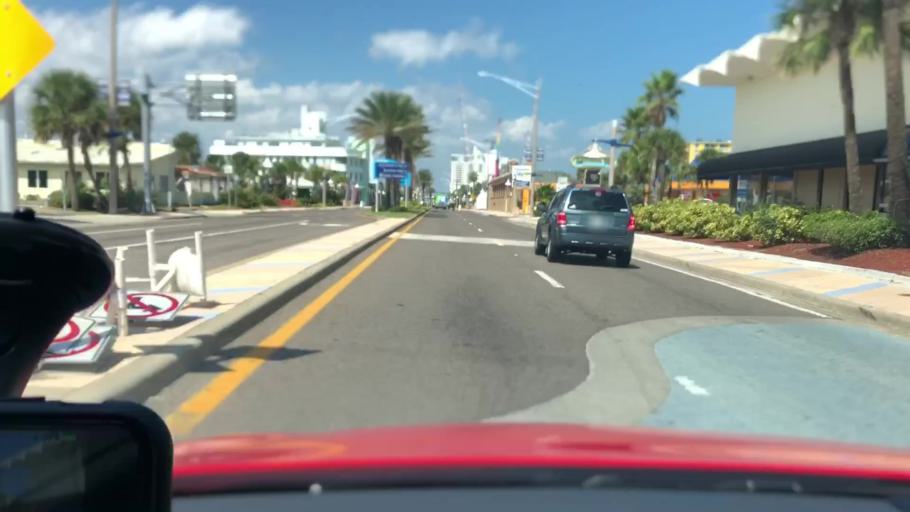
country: US
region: Florida
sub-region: Volusia County
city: Daytona Beach
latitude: 29.2221
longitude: -81.0058
